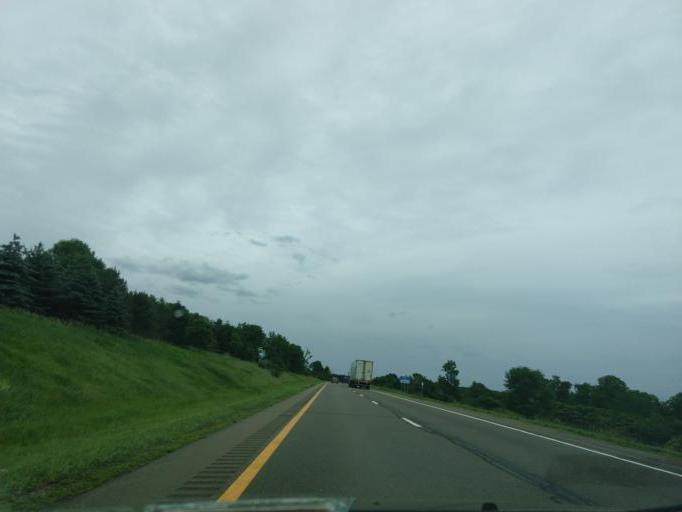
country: US
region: New York
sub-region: Chenango County
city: Lakeview
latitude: 42.3925
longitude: -76.0024
